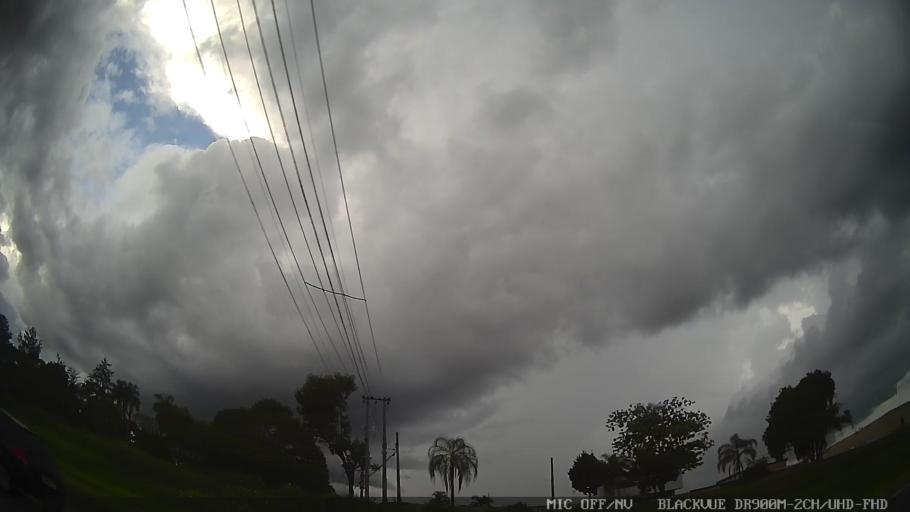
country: BR
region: Sao Paulo
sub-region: Campinas
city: Campinas
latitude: -22.8385
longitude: -47.0353
